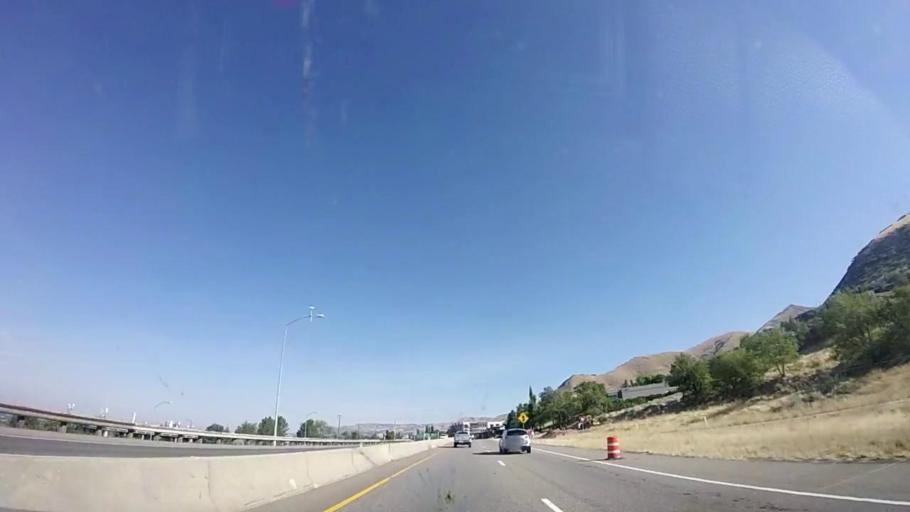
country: US
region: Utah
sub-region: Salt Lake County
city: Canyon Rim
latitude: 40.7171
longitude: -111.8091
